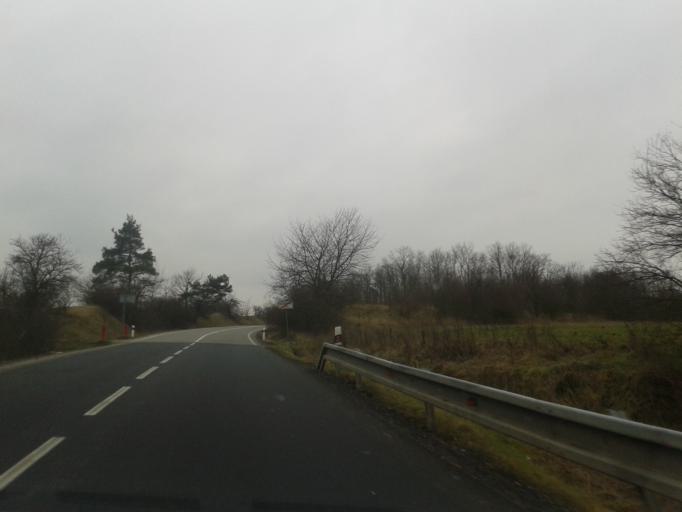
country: CZ
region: Olomoucky
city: Namest' na Hane
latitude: 49.5780
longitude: 17.0443
